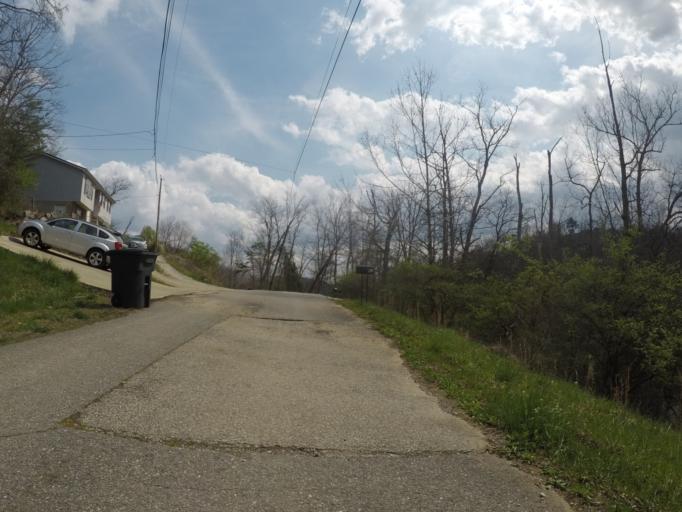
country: US
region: West Virginia
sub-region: Cabell County
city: Pea Ridge
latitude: 38.3979
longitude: -82.3361
